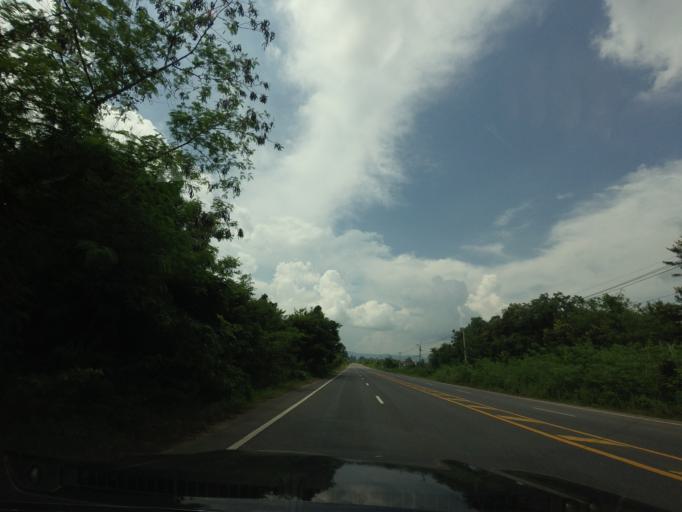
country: TH
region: Khon Kaen
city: Wiang Kao
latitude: 16.6747
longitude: 102.3246
